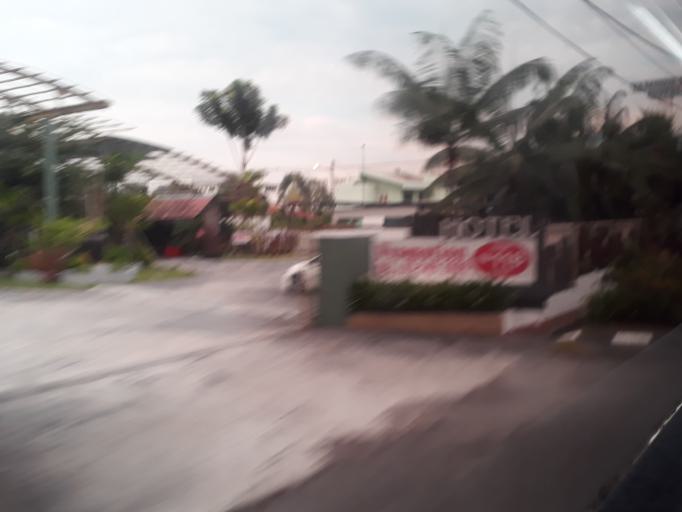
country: MY
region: Perak
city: Ipoh
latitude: 4.6015
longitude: 101.1163
